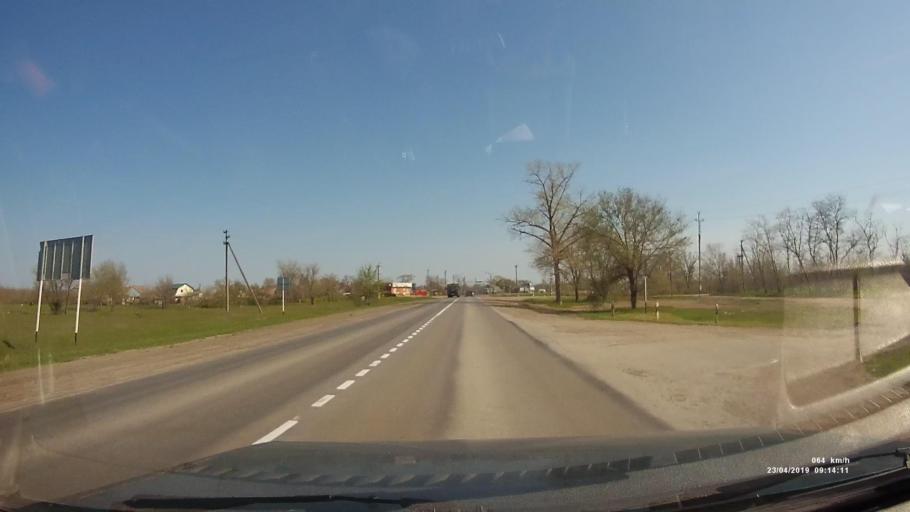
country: RU
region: Rostov
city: Proletarsk
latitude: 46.6231
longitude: 41.6533
